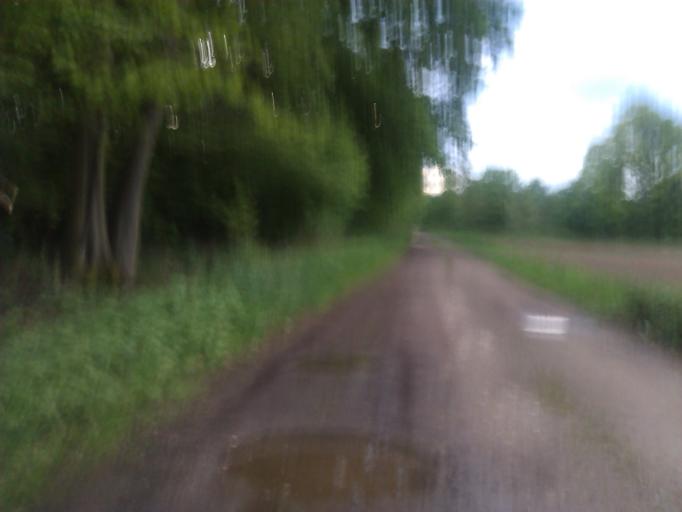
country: FR
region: Alsace
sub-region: Departement du Haut-Rhin
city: Ostheim
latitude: 48.1409
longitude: 7.3621
